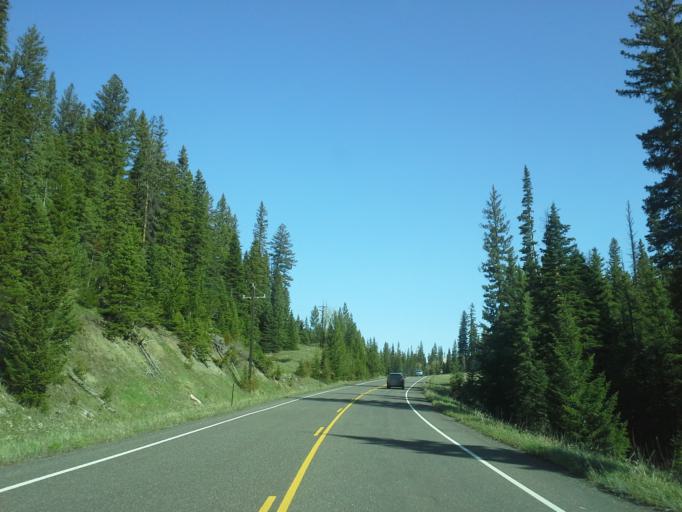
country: US
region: Montana
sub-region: Carbon County
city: Red Lodge
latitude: 44.9702
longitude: -109.8295
